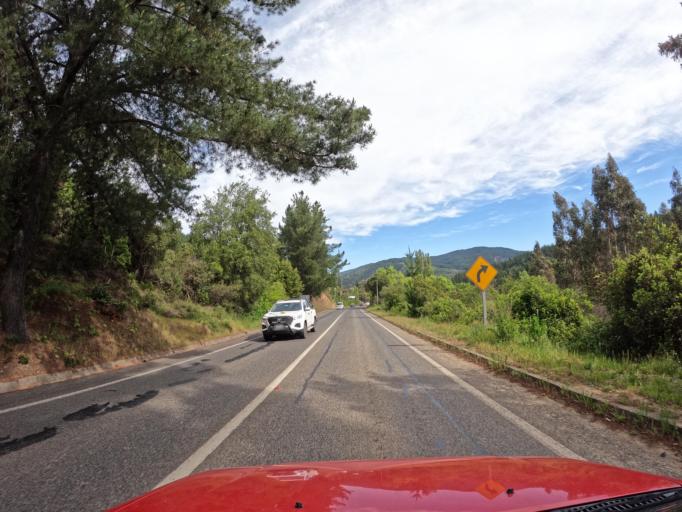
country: CL
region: Maule
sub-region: Provincia de Talca
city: Talca
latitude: -35.3050
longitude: -71.9647
